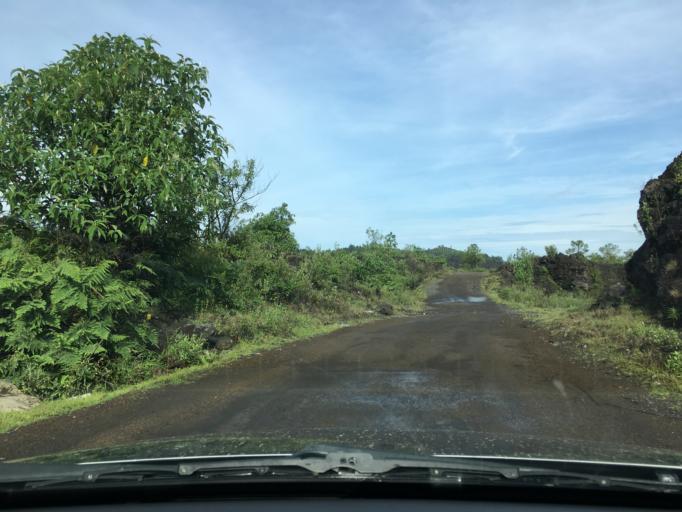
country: MX
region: Michoacan
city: Angahuan
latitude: 19.5189
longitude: -102.2217
